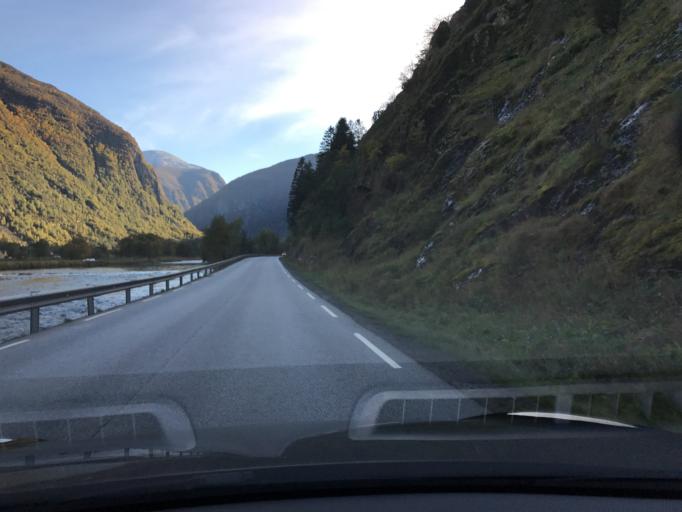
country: NO
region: Sogn og Fjordane
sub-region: Laerdal
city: Laerdalsoyri
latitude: 61.0957
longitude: 7.5180
